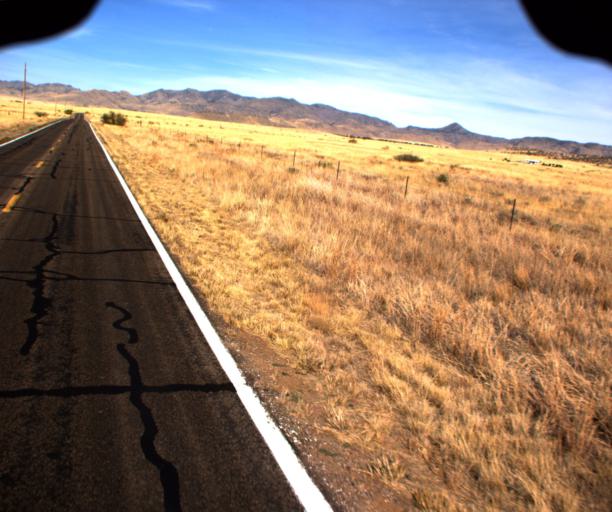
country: US
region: Arizona
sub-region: Cochise County
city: Willcox
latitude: 31.9874
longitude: -109.4539
